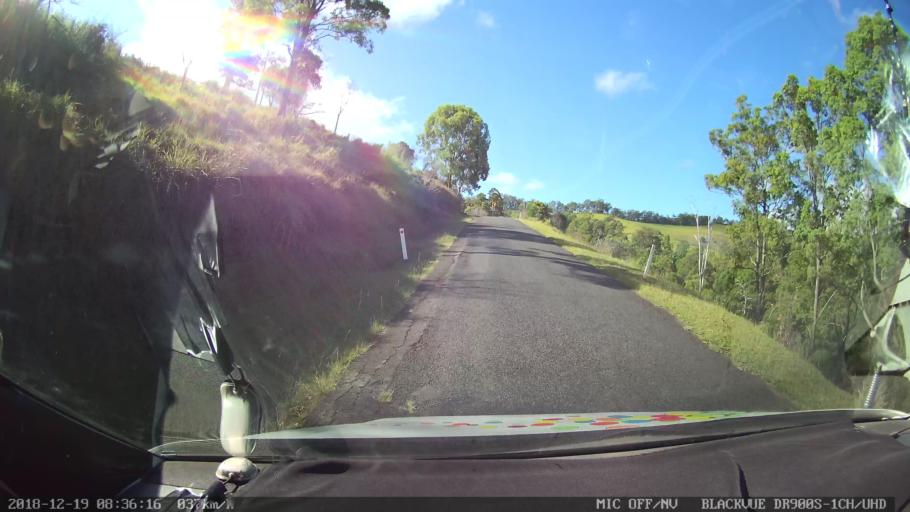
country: AU
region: New South Wales
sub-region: Kyogle
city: Kyogle
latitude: -28.3250
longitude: 152.9729
